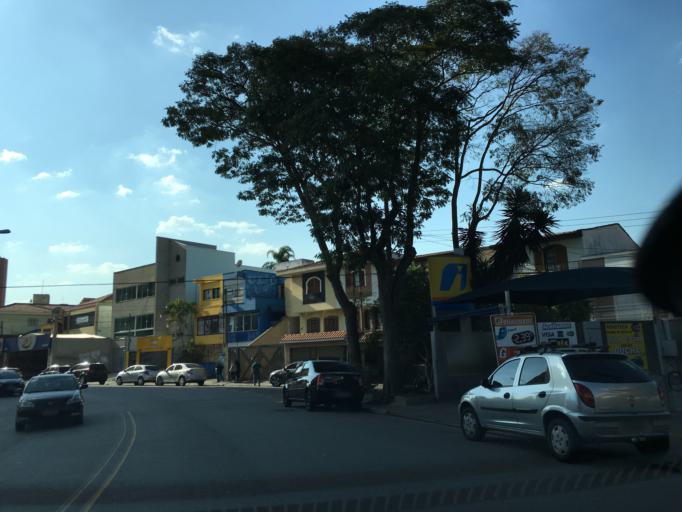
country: BR
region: Sao Paulo
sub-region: Sao Paulo
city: Sao Paulo
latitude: -23.4712
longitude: -46.6298
